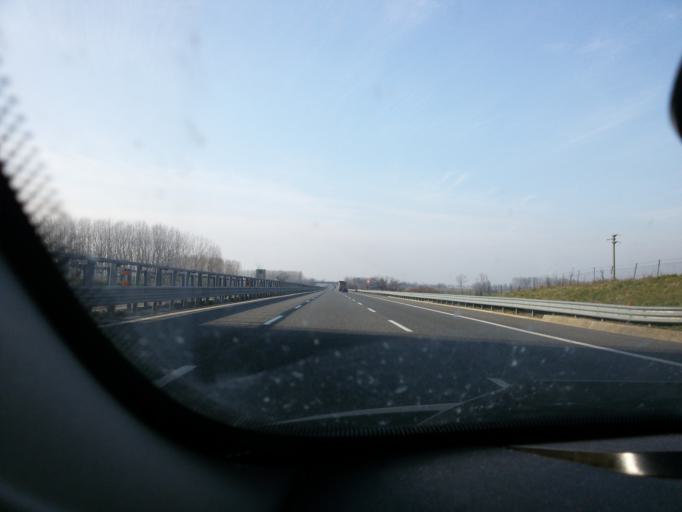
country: IT
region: Piedmont
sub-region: Provincia di Alessandria
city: Mirabello Monferrato
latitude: 45.0383
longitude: 8.5307
